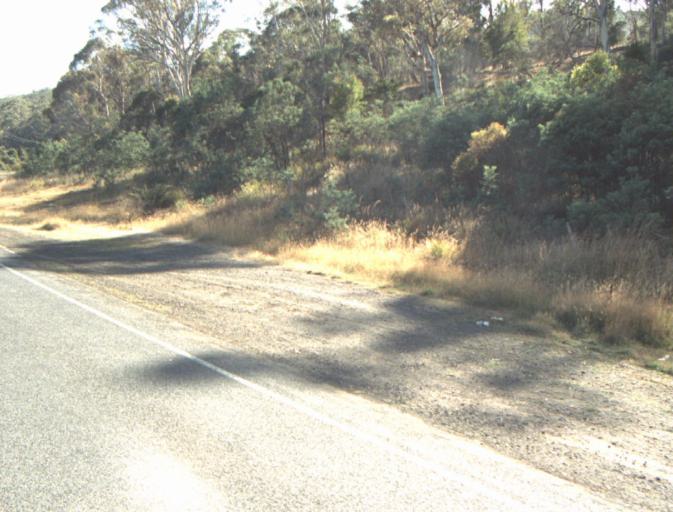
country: AU
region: Tasmania
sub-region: Launceston
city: Newstead
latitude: -41.4295
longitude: 147.2523
